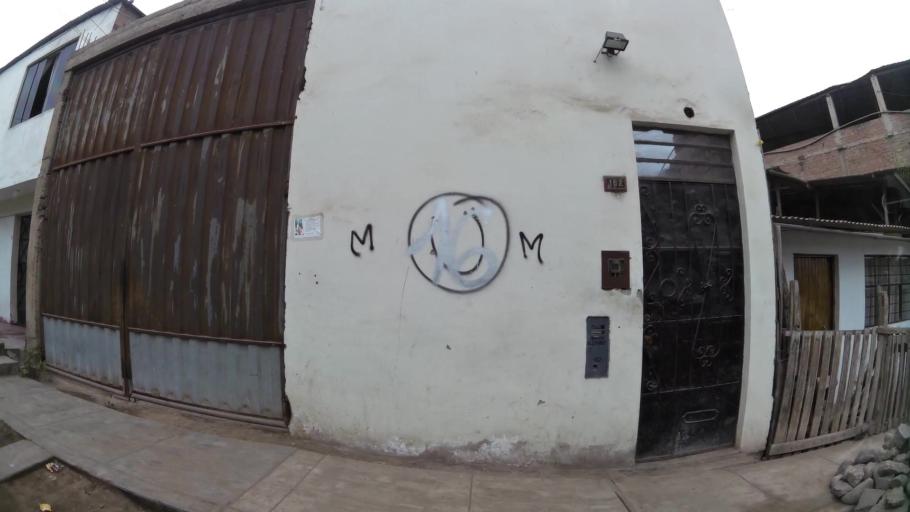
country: PE
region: Lima
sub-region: Lima
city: Surco
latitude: -12.1773
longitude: -76.9495
